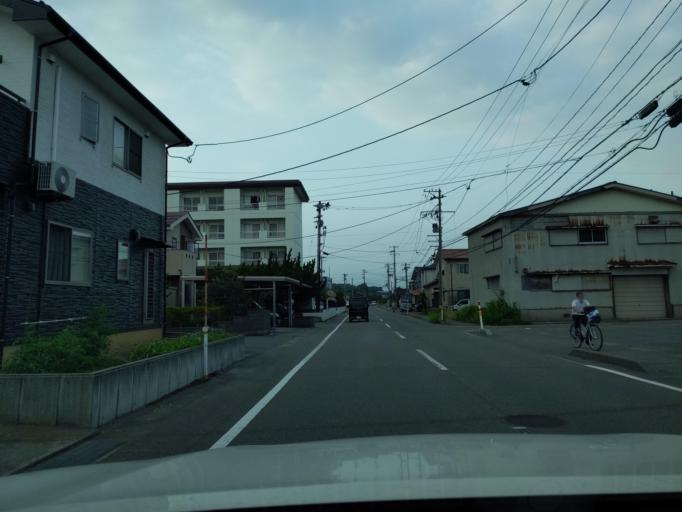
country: JP
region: Niigata
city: Kashiwazaki
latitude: 37.4152
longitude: 138.6116
